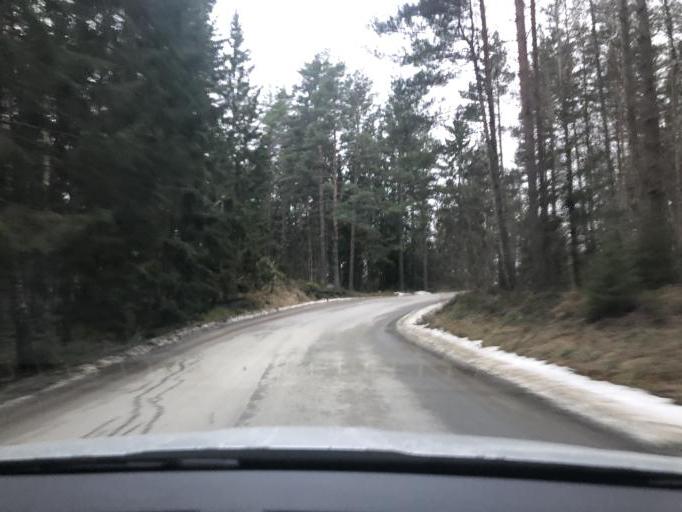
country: SE
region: Stockholm
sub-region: Botkyrka Kommun
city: Tullinge
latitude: 59.1638
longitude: 17.8957
